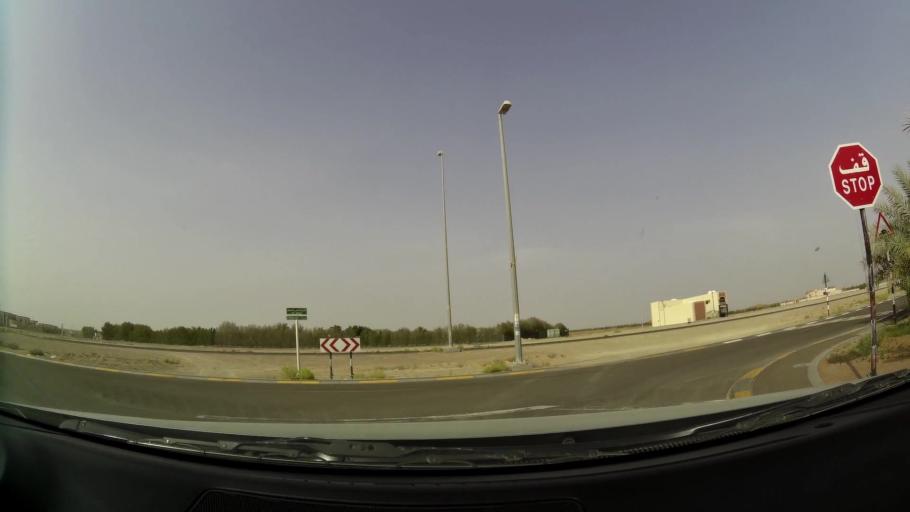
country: AE
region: Abu Dhabi
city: Al Ain
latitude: 24.2128
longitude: 55.5971
